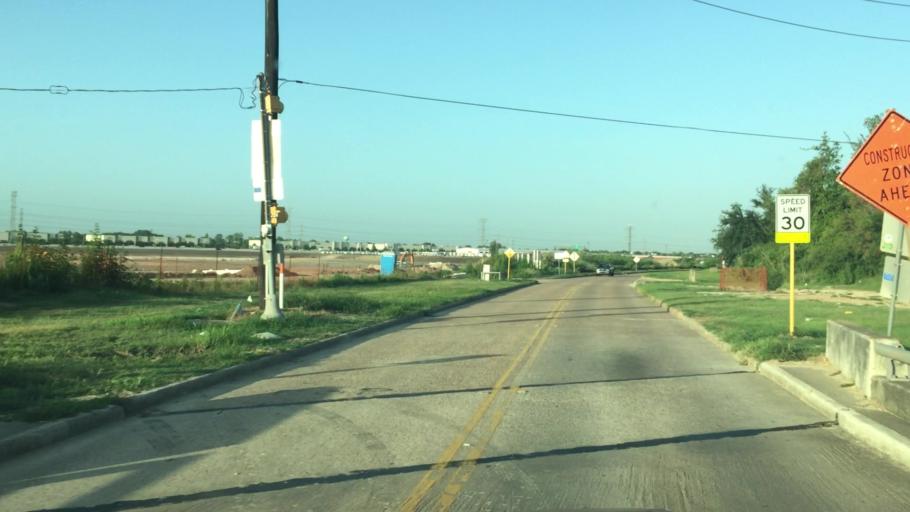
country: US
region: Texas
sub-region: Harris County
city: Hudson
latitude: 29.9446
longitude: -95.4744
